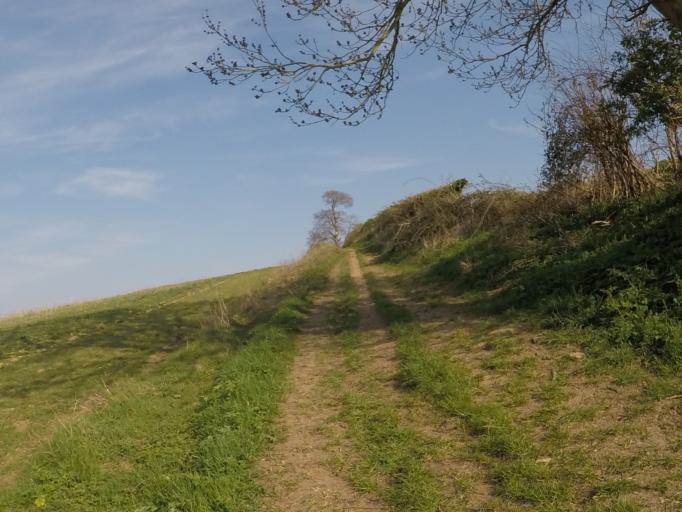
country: GB
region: England
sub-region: Oxfordshire
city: Charlbury
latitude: 51.8767
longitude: -1.5109
